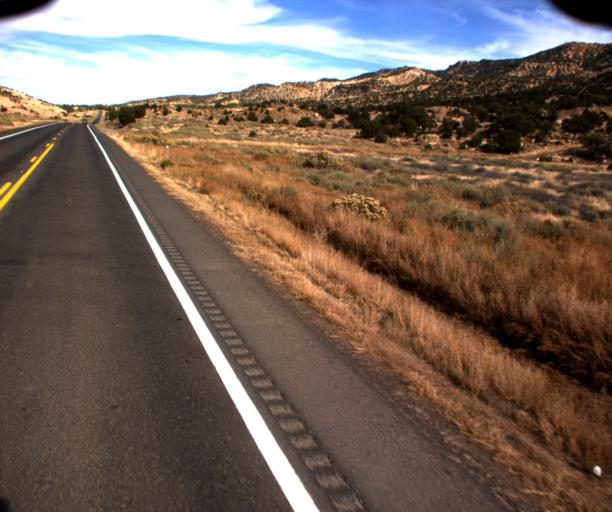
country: US
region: Arizona
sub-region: Navajo County
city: Kayenta
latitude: 36.6300
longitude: -110.4524
